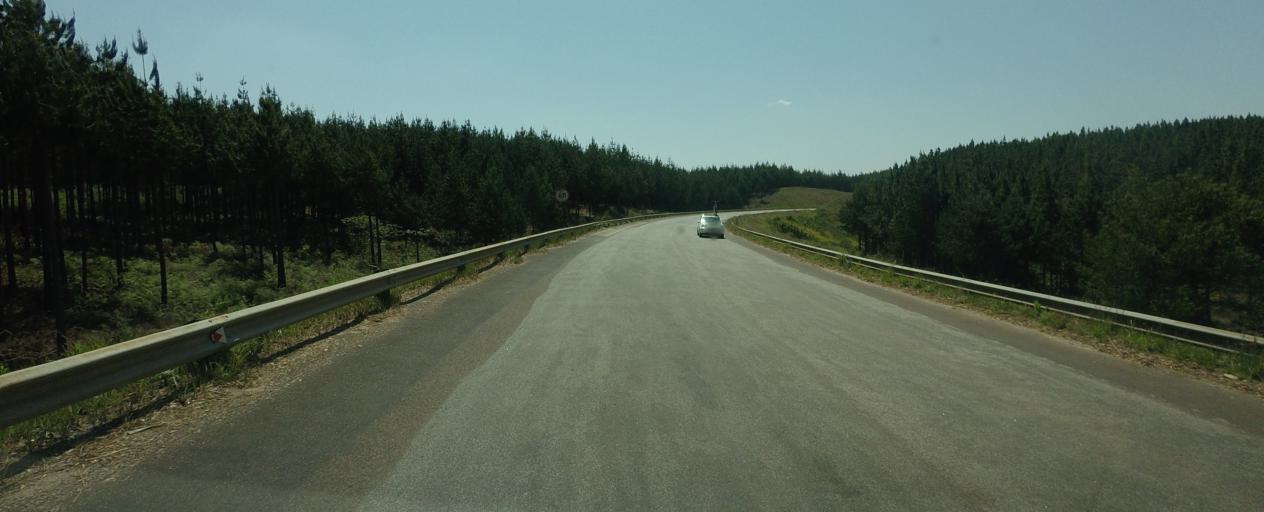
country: ZA
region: Mpumalanga
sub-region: Ehlanzeni District
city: Graksop
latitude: -24.9120
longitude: 30.8420
